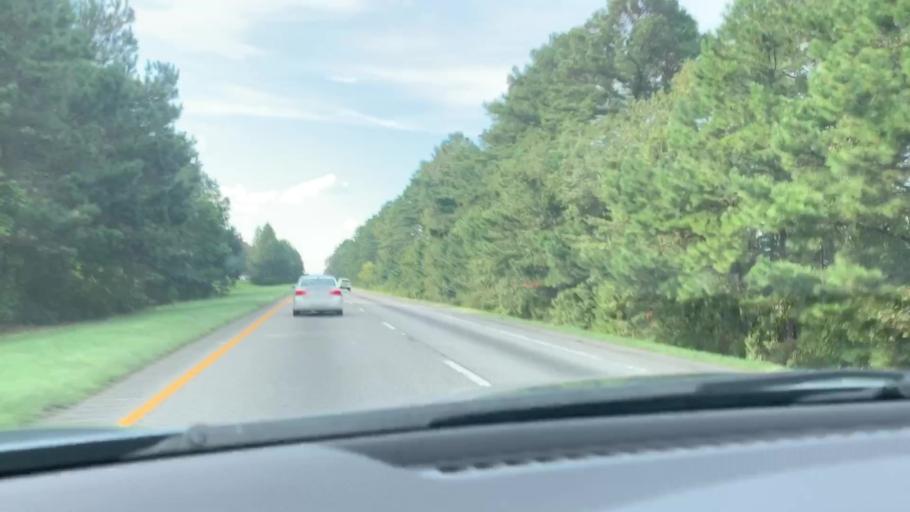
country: US
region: South Carolina
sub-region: Orangeburg County
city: Brookdale
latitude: 33.4363
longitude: -80.7001
